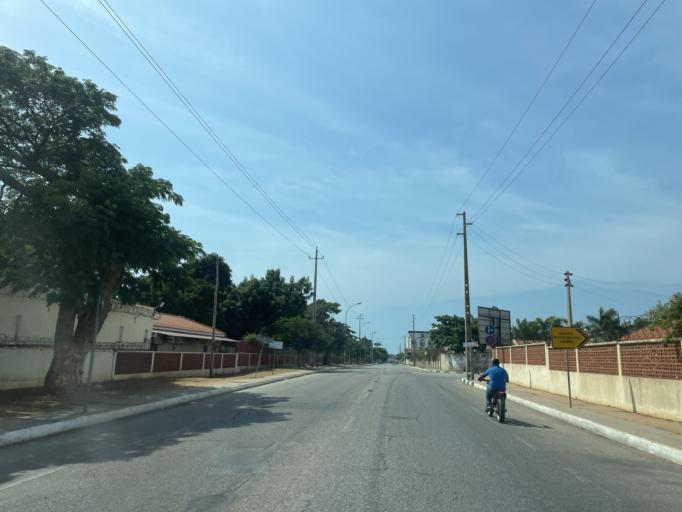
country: AO
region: Luanda
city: Luanda
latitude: -8.9122
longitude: 13.1838
